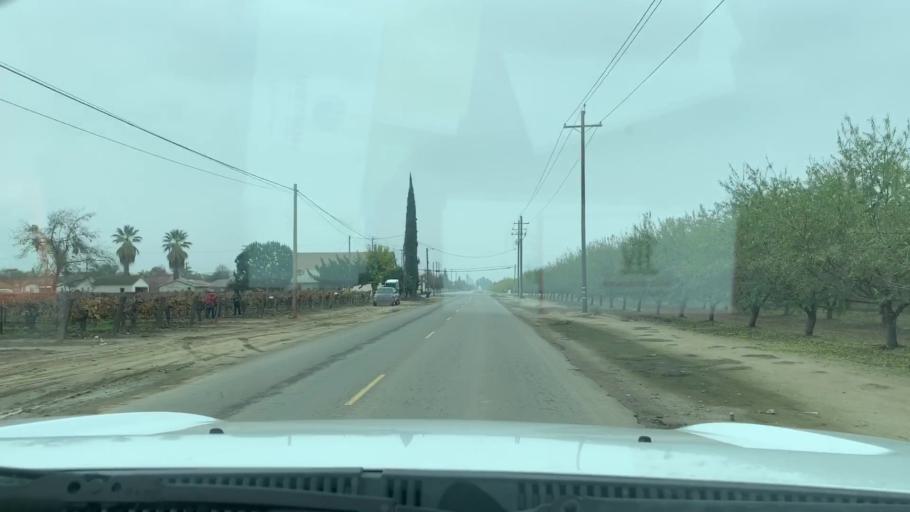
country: US
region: California
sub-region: Kern County
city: Shafter
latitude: 35.5017
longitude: -119.2961
